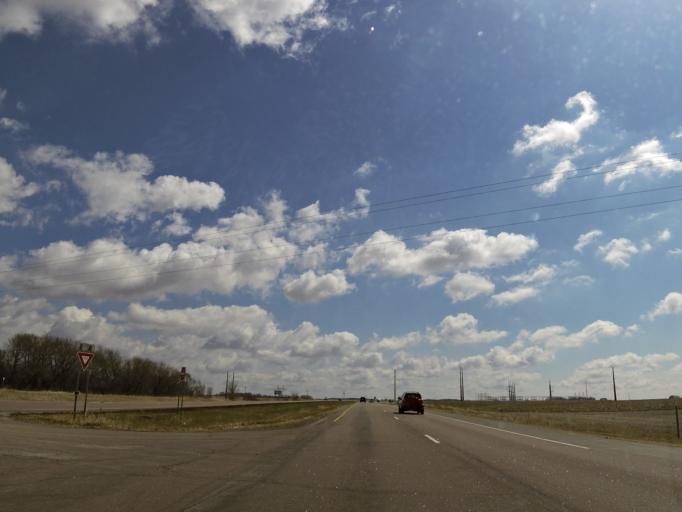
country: US
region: Minnesota
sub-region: Dakota County
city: Farmington
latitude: 44.6449
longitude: -92.9973
